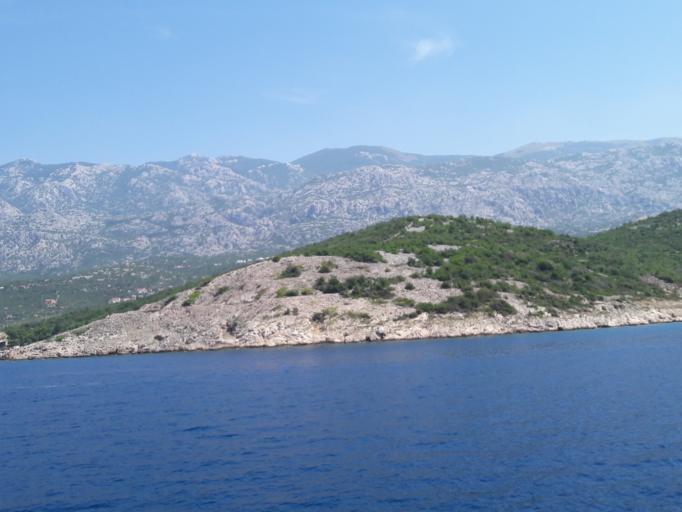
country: HR
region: Primorsko-Goranska
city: Banjol
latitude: 44.7161
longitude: 14.8859
